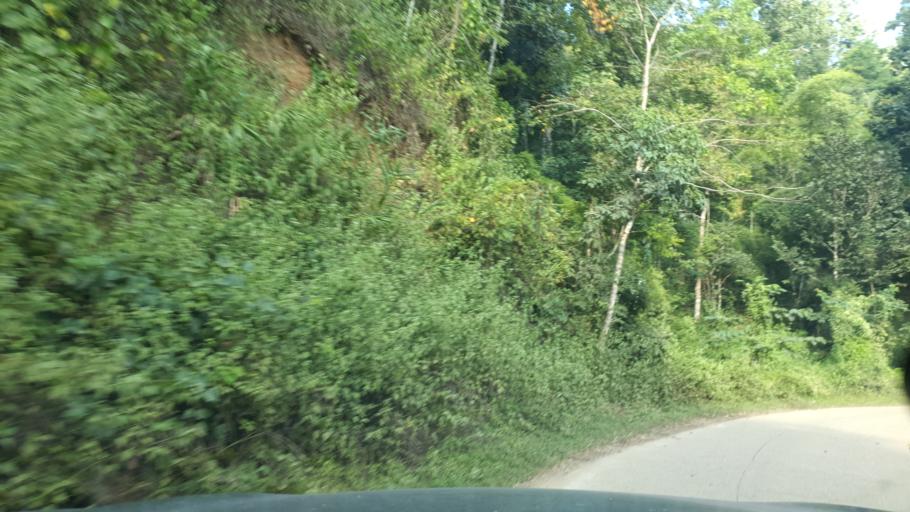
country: TH
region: Chiang Mai
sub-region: Amphoe Chiang Dao
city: Chiang Dao
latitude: 19.4122
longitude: 98.7965
